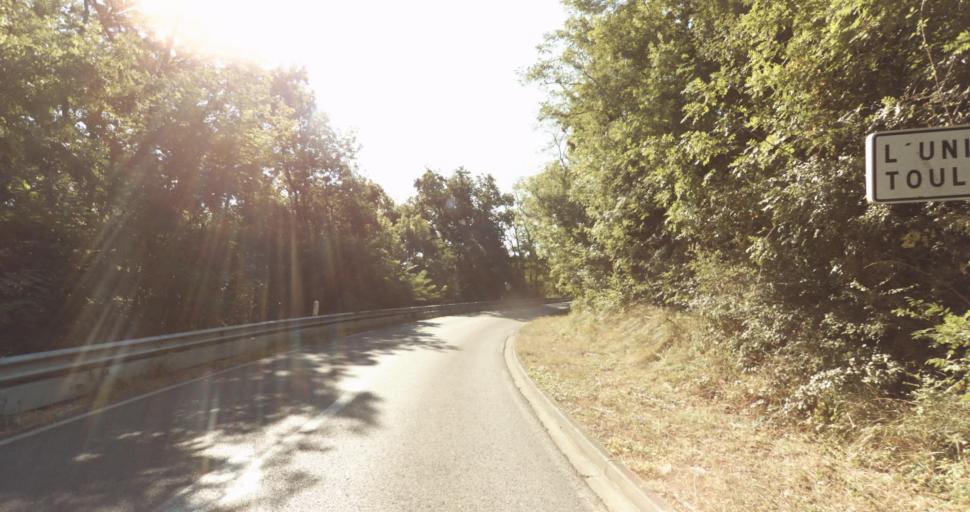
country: FR
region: Midi-Pyrenees
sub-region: Departement de la Haute-Garonne
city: Saint-Genies-Bellevue
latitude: 43.6761
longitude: 1.4788
